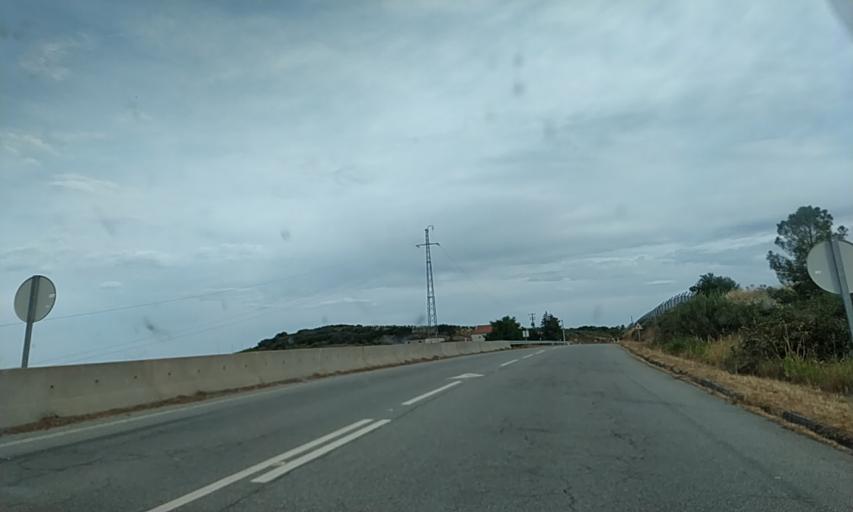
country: PT
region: Viseu
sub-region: Sao Joao da Pesqueira
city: Sao Joao da Pesqueira
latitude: 41.1270
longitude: -7.3938
